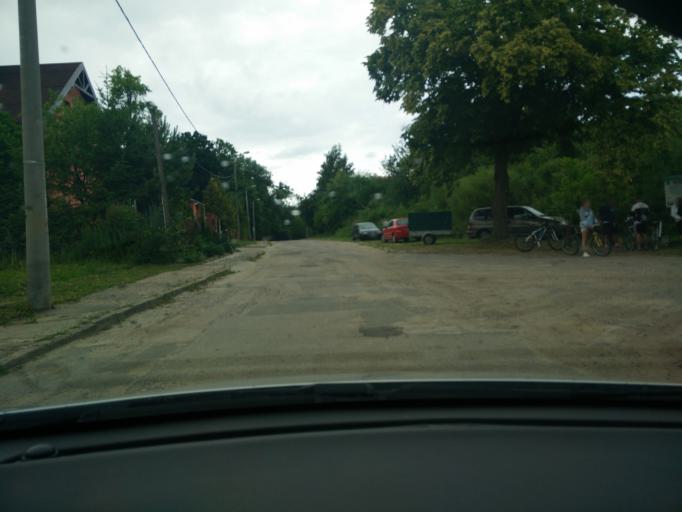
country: PL
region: Pomeranian Voivodeship
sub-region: Powiat pucki
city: Mrzezino
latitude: 54.6647
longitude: 18.4563
